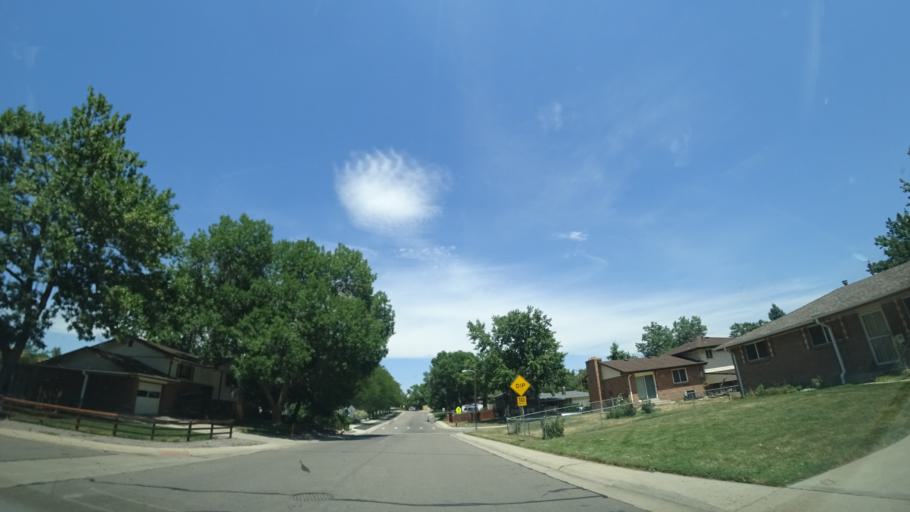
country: US
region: Colorado
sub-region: Jefferson County
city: Lakewood
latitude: 39.6925
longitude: -105.0960
